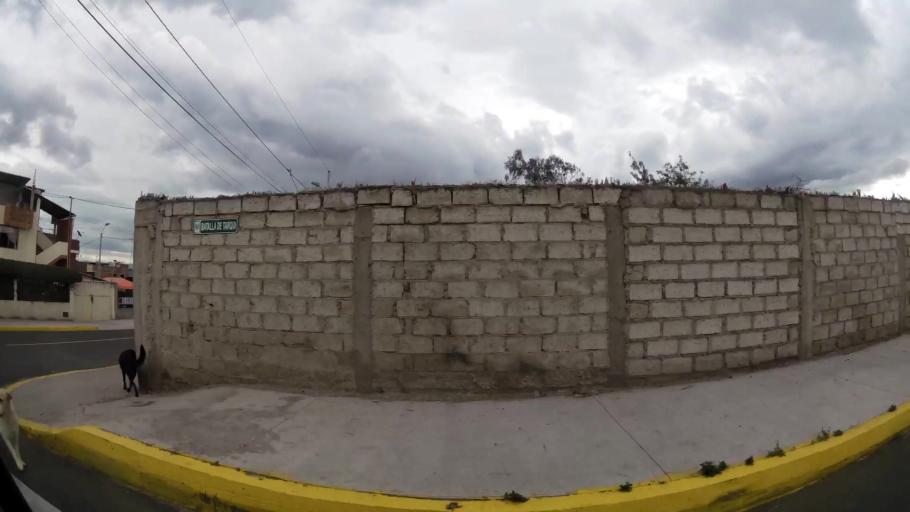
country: EC
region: Tungurahua
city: Ambato
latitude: -1.2619
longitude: -78.6155
